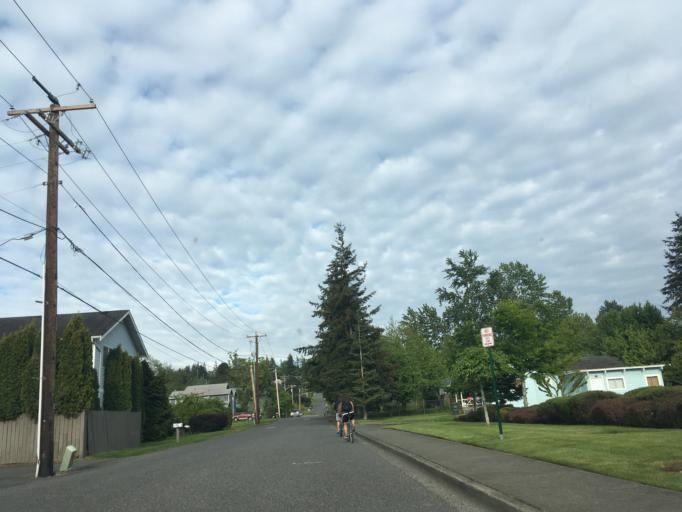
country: US
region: Washington
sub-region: Whatcom County
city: Geneva
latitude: 48.7617
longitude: -122.4423
